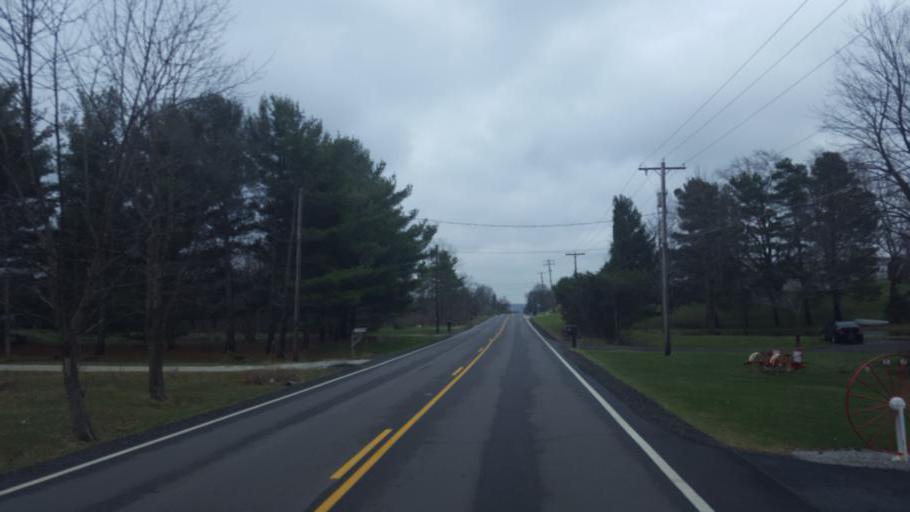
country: US
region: Ohio
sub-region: Medina County
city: Medina
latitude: 41.1066
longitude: -81.8519
